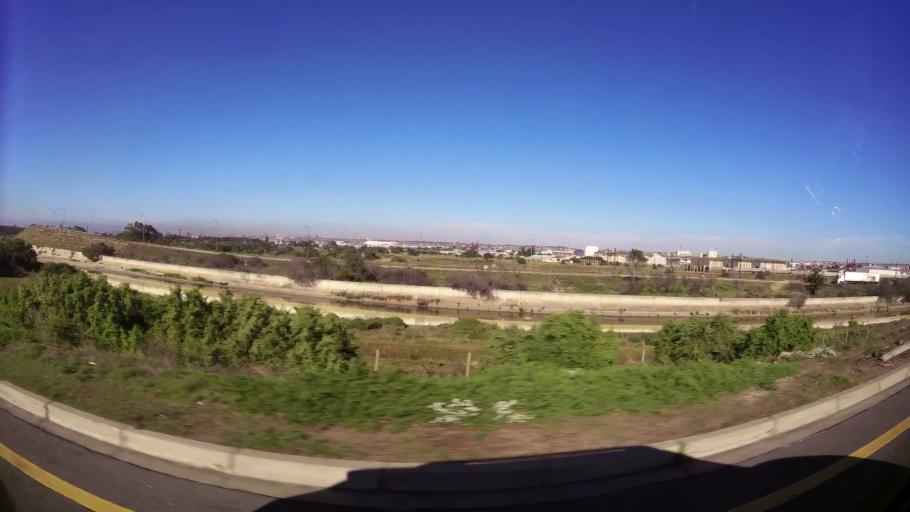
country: ZA
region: Eastern Cape
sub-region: Nelson Mandela Bay Metropolitan Municipality
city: Port Elizabeth
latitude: -33.9148
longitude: 25.6076
